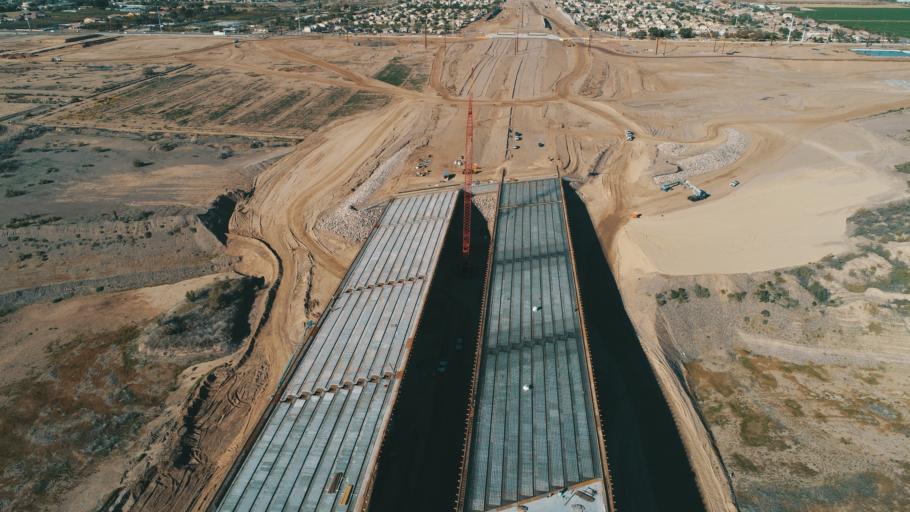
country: US
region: Arizona
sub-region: Maricopa County
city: Laveen
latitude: 33.4005
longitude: -112.1920
